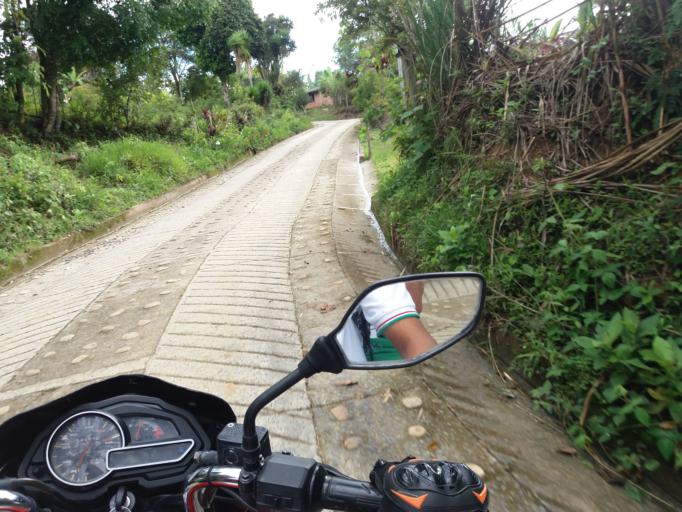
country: CO
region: Santander
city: Guepsa
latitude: 6.0028
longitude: -73.5437
